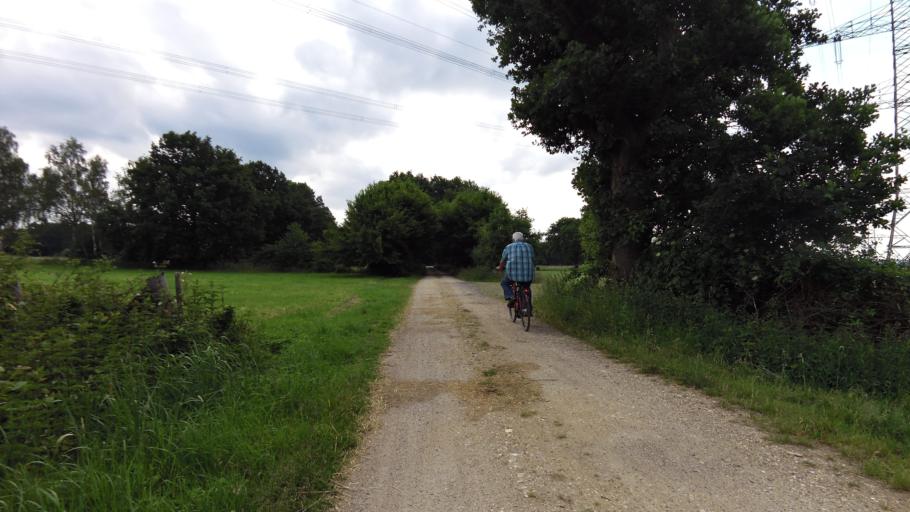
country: DE
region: North Rhine-Westphalia
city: Meckenheim
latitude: 50.6662
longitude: 7.0089
